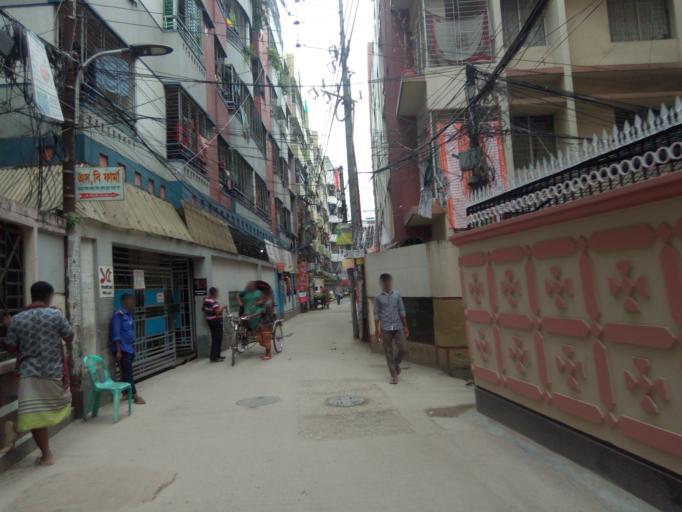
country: BD
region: Dhaka
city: Paltan
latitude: 23.7454
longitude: 90.4097
